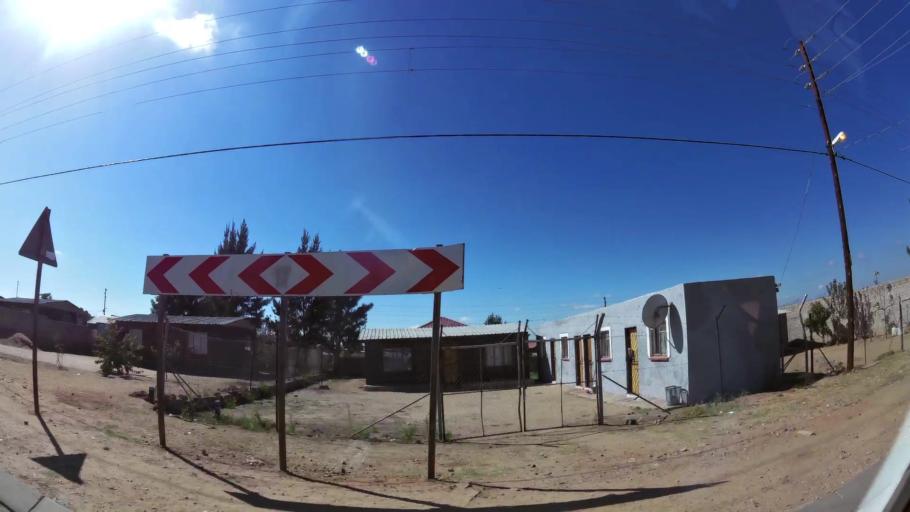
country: ZA
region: Limpopo
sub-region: Capricorn District Municipality
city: Polokwane
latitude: -23.8852
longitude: 29.4093
